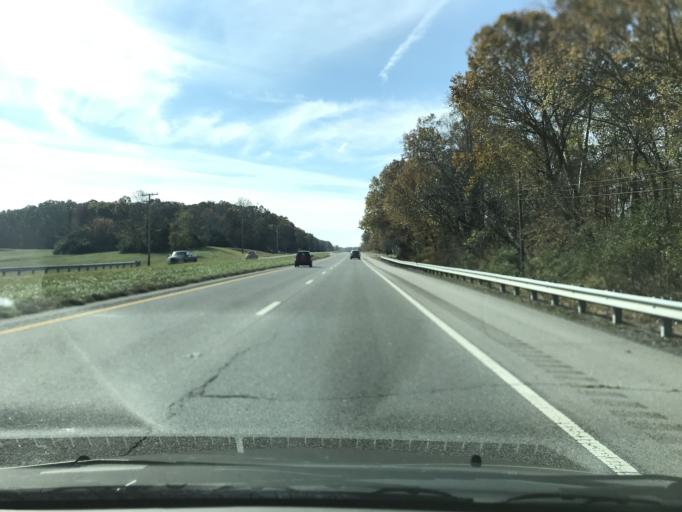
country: US
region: Tennessee
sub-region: Coffee County
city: Manchester
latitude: 35.4239
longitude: -86.1112
